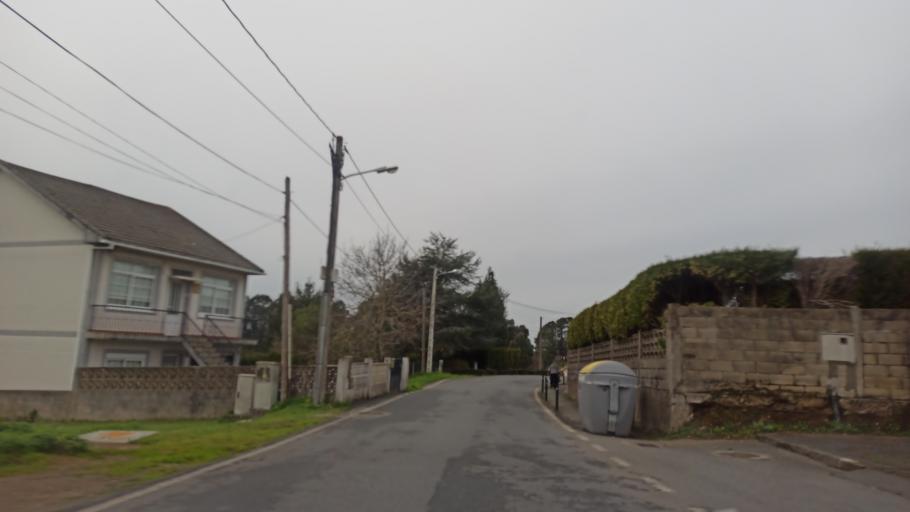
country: ES
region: Galicia
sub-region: Provincia da Coruna
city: Oleiros
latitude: 43.3912
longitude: -8.3125
